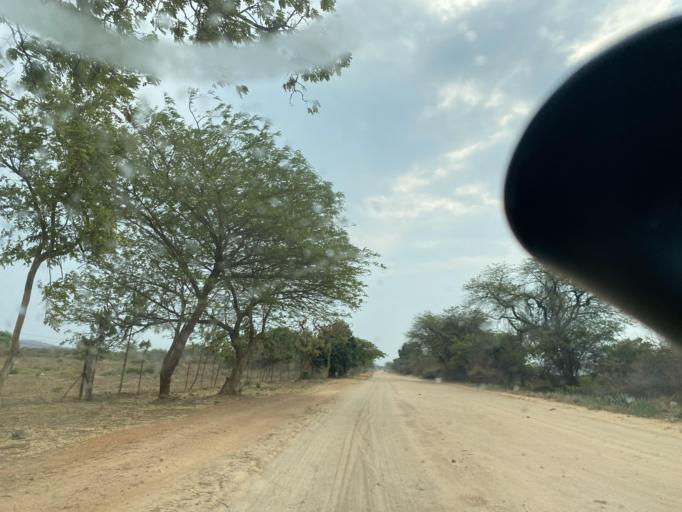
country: ZM
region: Lusaka
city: Lusaka
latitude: -15.2859
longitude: 28.2960
